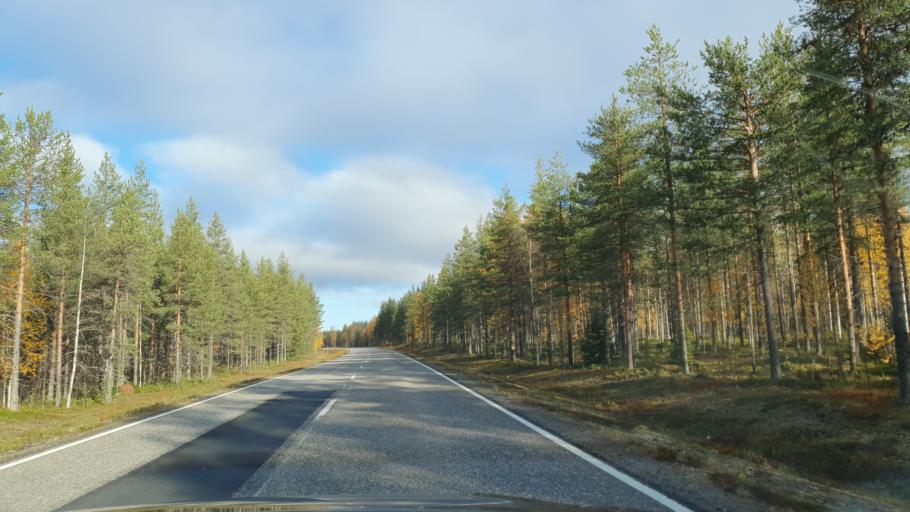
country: FI
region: Lapland
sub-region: Tunturi-Lappi
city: Kittilae
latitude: 67.1866
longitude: 24.9358
